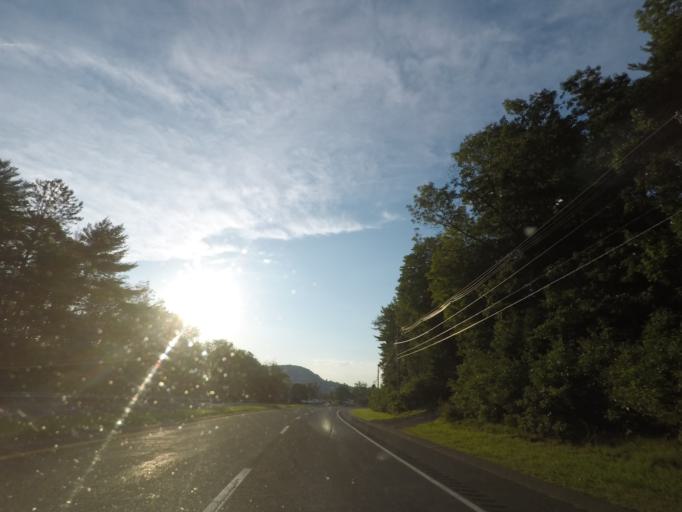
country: US
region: Massachusetts
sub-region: Hampden County
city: Brimfield
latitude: 42.1203
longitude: -72.2481
